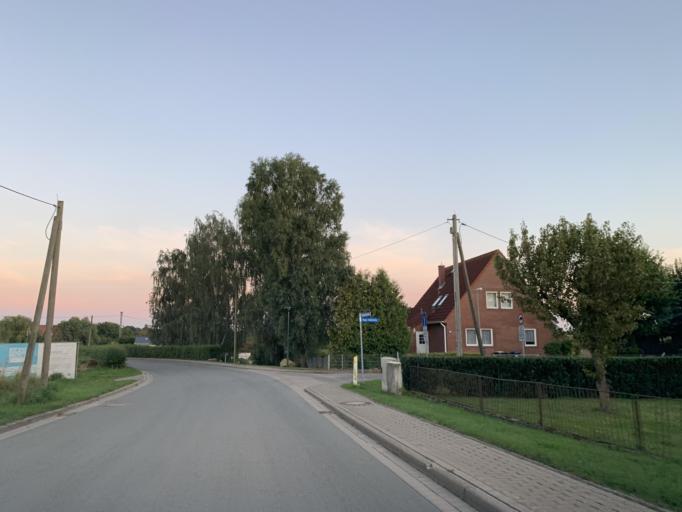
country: DE
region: Mecklenburg-Vorpommern
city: Blankensee
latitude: 53.4417
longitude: 13.3008
